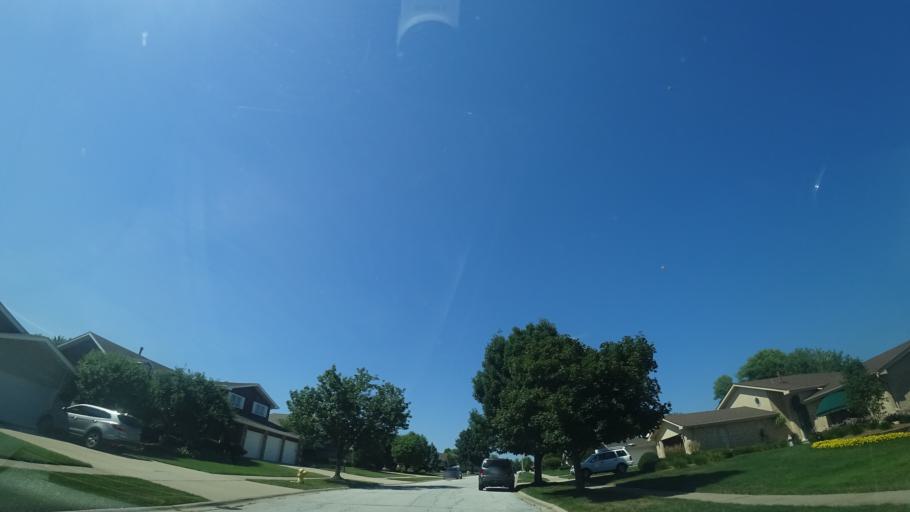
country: US
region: Illinois
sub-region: Will County
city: Mokena
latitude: 41.5667
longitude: -87.9058
